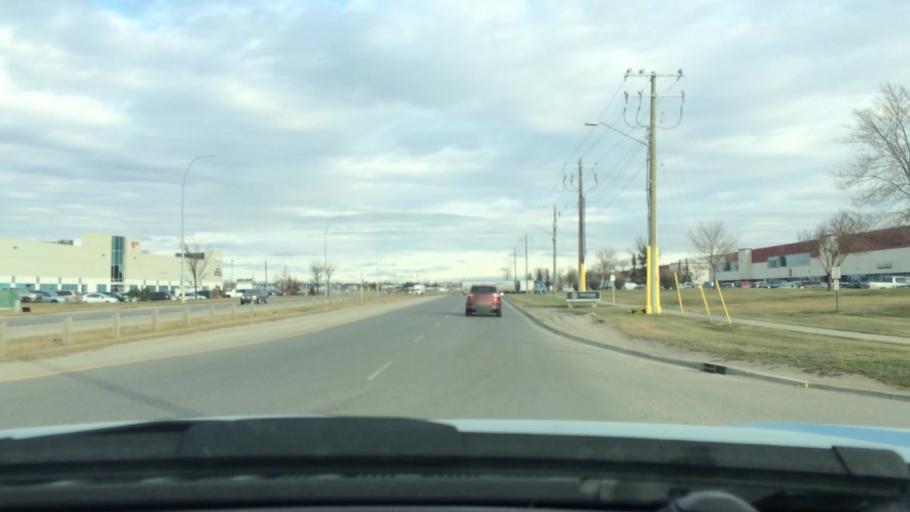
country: CA
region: Alberta
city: Calgary
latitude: 51.0089
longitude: -113.9583
